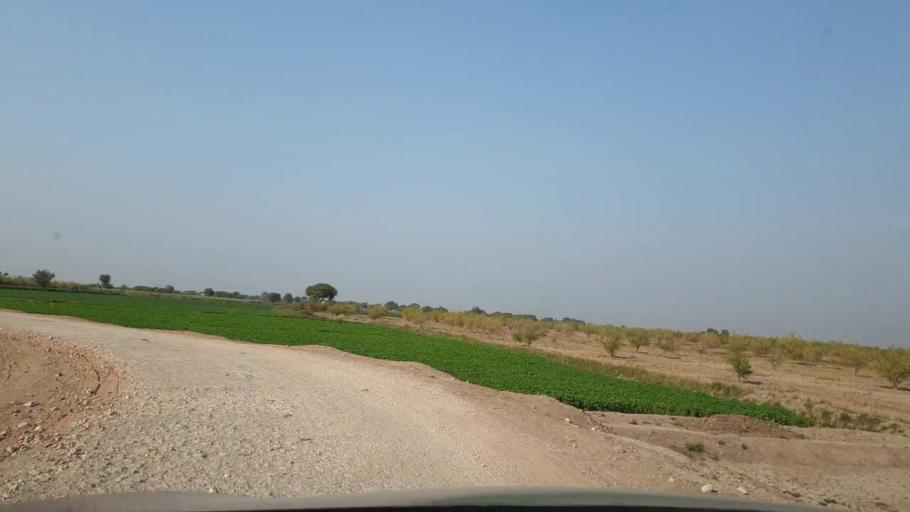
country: PK
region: Sindh
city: Tando Allahyar
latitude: 25.5765
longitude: 68.7951
